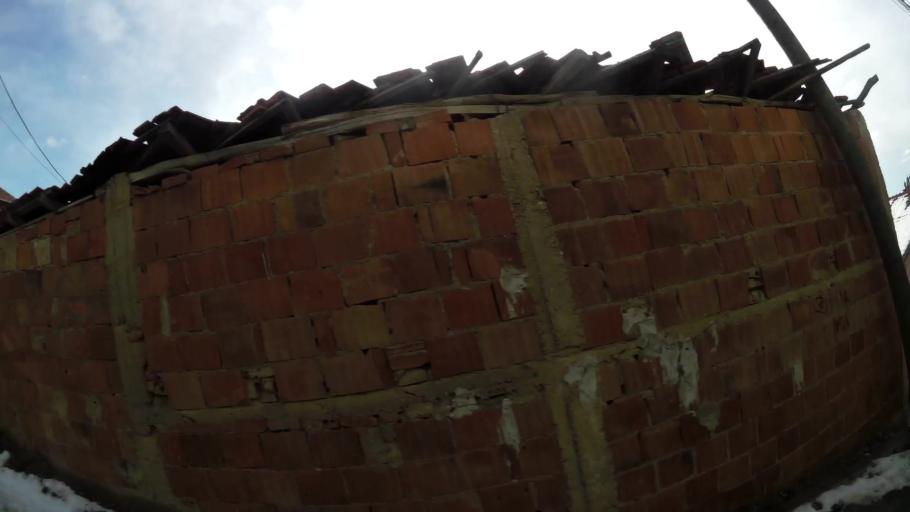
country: XK
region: Pristina
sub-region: Komuna e Prishtines
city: Pristina
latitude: 42.6719
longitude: 21.1788
